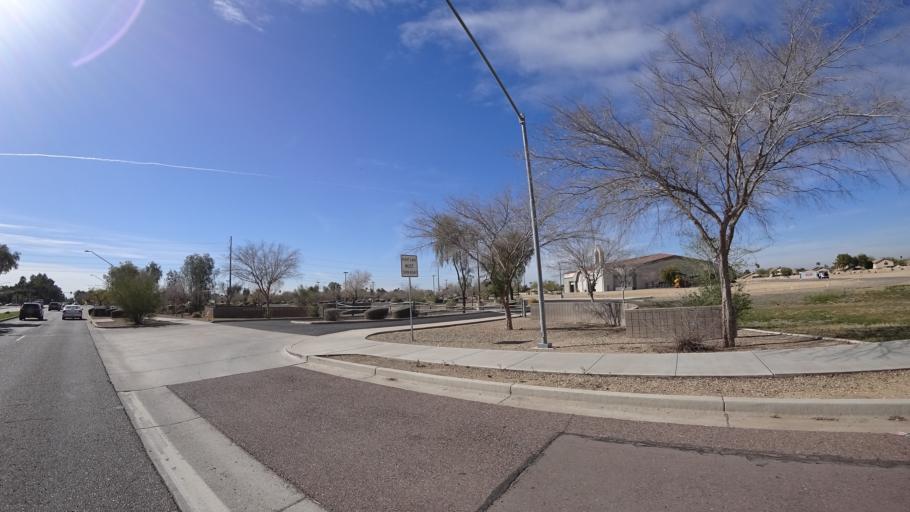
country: US
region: Arizona
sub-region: Maricopa County
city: Peoria
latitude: 33.5983
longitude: -112.1861
